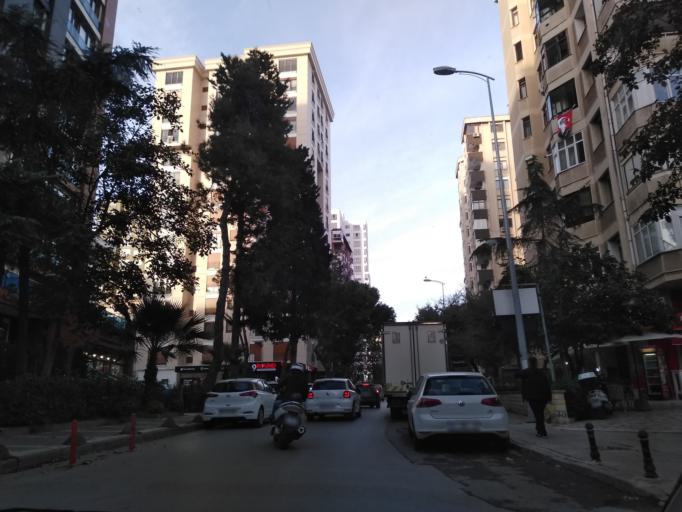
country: TR
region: Istanbul
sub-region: Atasehir
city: Atasehir
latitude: 40.9681
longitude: 29.0883
